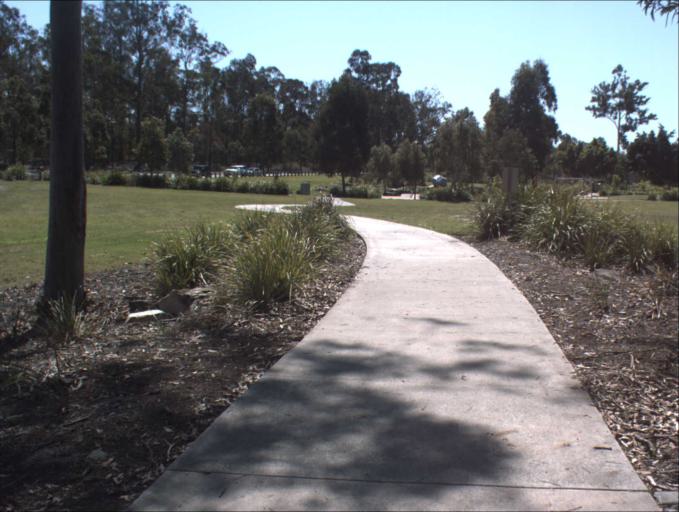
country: AU
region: Queensland
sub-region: Logan
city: Waterford West
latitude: -27.7165
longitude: 153.1462
